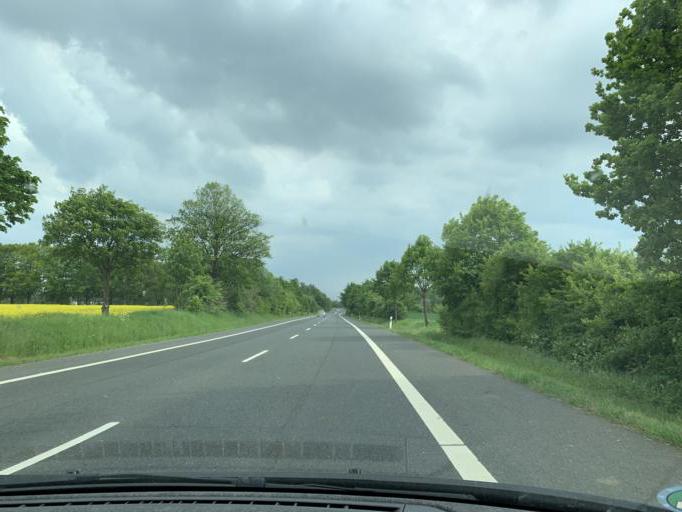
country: DE
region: North Rhine-Westphalia
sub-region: Regierungsbezirk Koln
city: Norvenich
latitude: 50.7658
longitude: 6.6336
